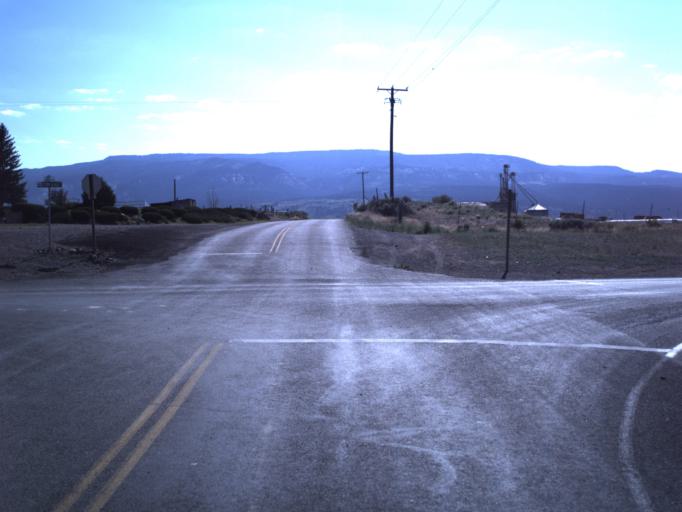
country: US
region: Utah
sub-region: Wayne County
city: Loa
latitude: 38.4116
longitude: -111.6209
